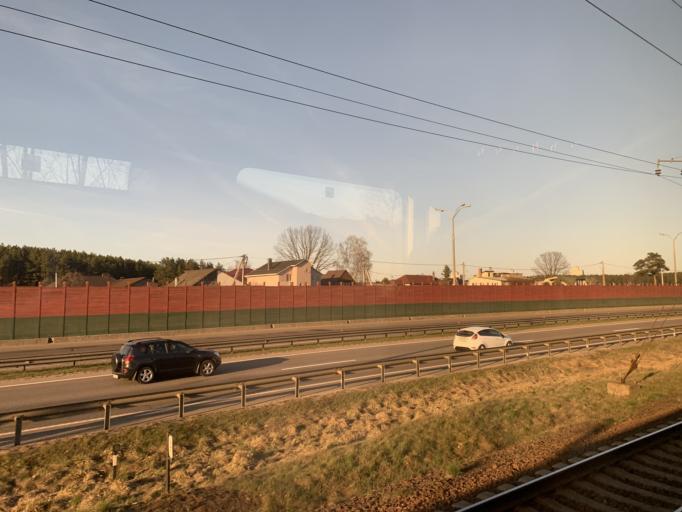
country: BY
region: Minsk
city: Zhdanovichy
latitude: 53.9516
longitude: 27.4121
